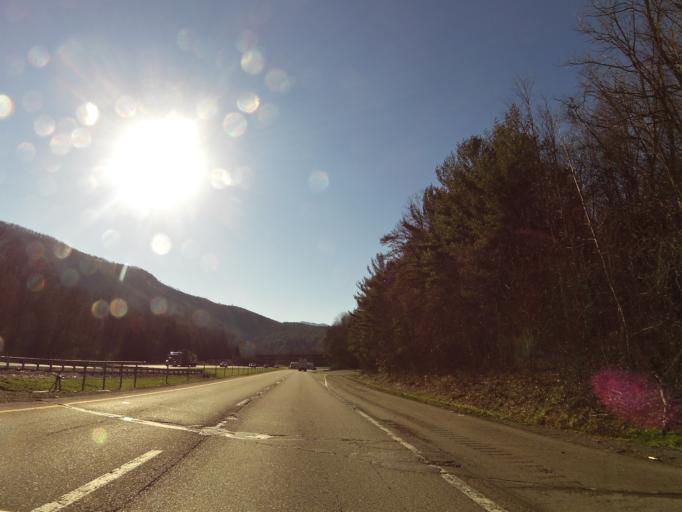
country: US
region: Tennessee
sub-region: Cocke County
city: Newport
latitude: 35.8414
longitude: -83.1816
